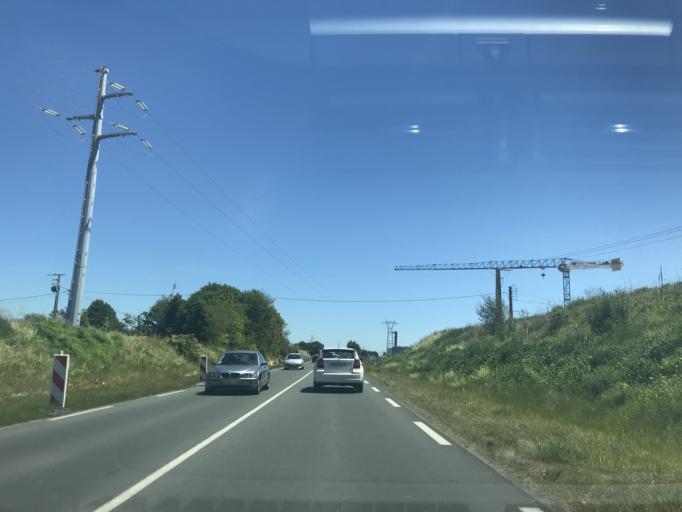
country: FR
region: Poitou-Charentes
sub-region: Departement de la Charente-Maritime
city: Royan
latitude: 45.6425
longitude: -1.0377
